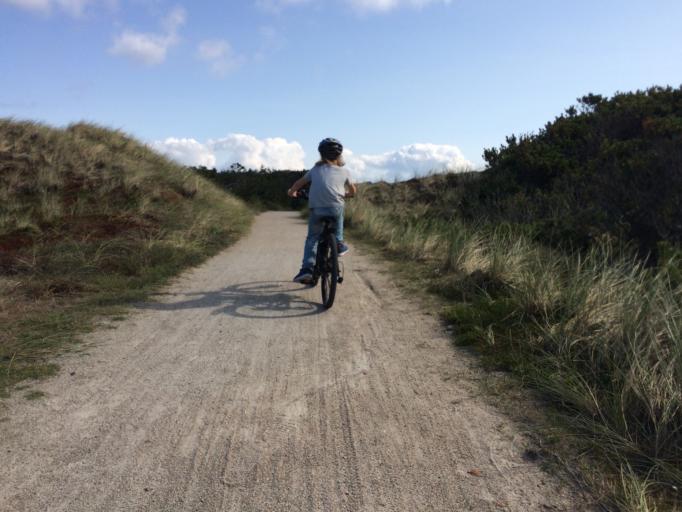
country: DK
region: Central Jutland
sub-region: Ringkobing-Skjern Kommune
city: Hvide Sande
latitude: 55.9447
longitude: 8.1490
